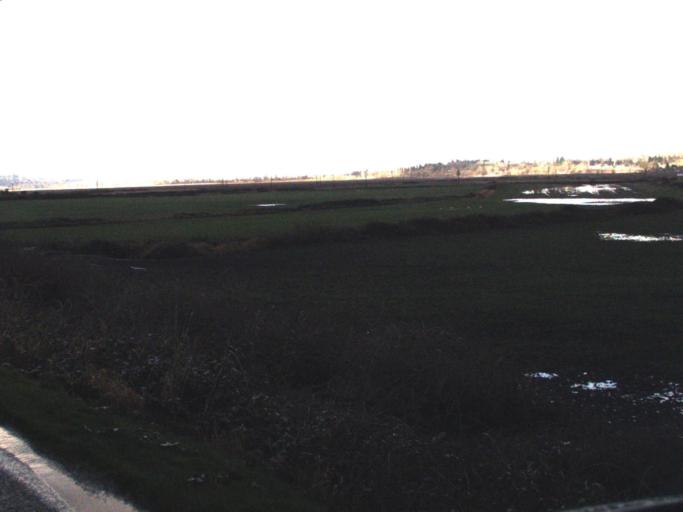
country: US
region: Washington
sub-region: Snohomish County
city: Silver Firs
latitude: 47.8881
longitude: -122.1383
